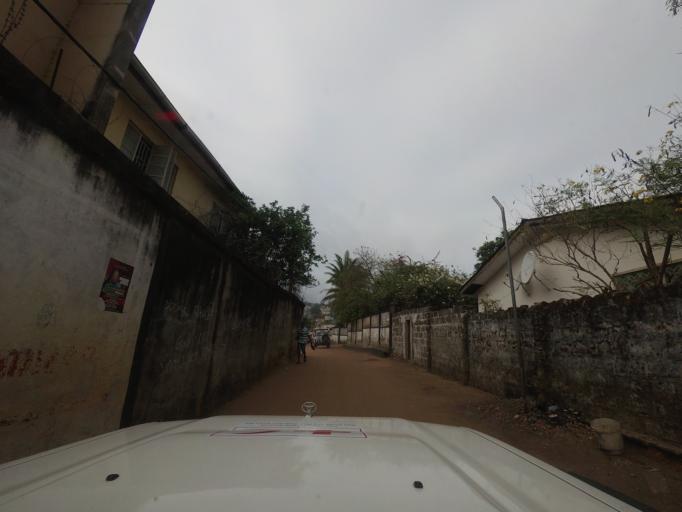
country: SL
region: Western Area
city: Freetown
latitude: 8.4891
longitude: -13.2649
